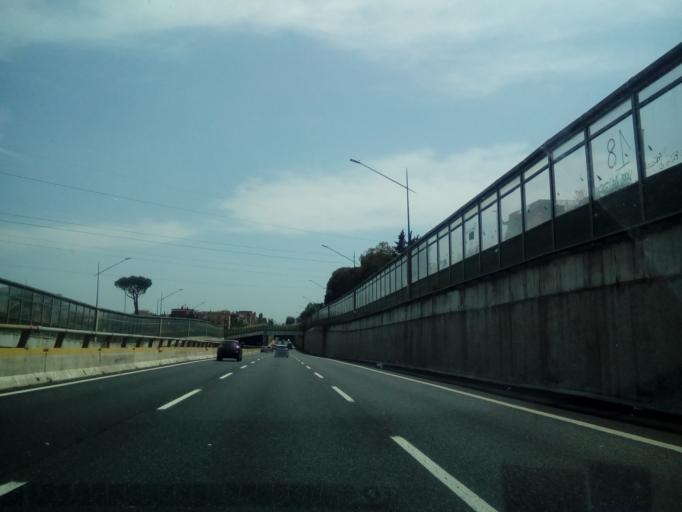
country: IT
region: Latium
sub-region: Citta metropolitana di Roma Capitale
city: Valle Santa
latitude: 41.9511
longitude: 12.3829
